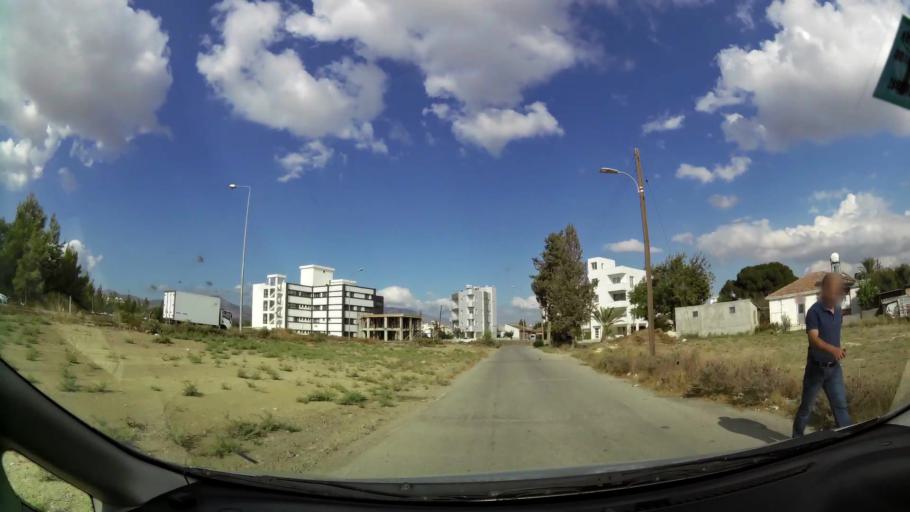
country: CY
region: Lefkosia
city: Nicosia
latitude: 35.1992
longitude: 33.3581
